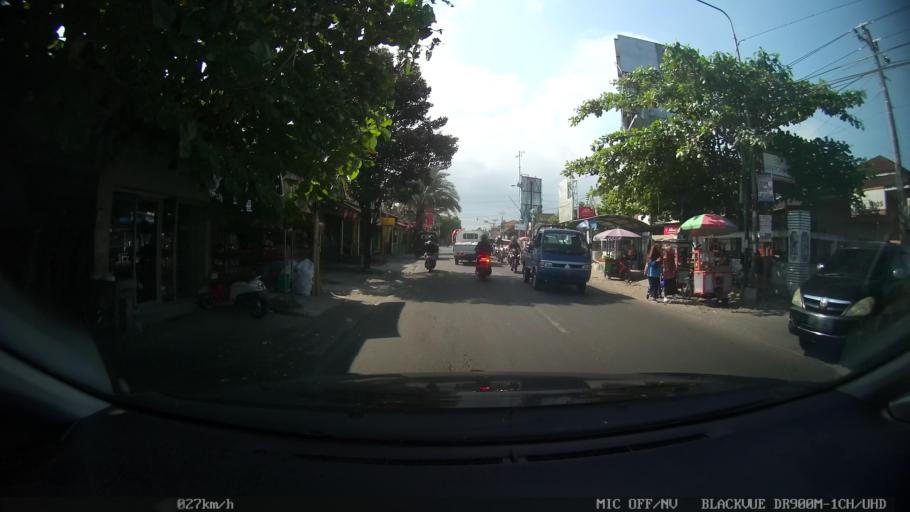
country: ID
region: Daerah Istimewa Yogyakarta
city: Sewon
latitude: -7.8709
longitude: 110.3912
